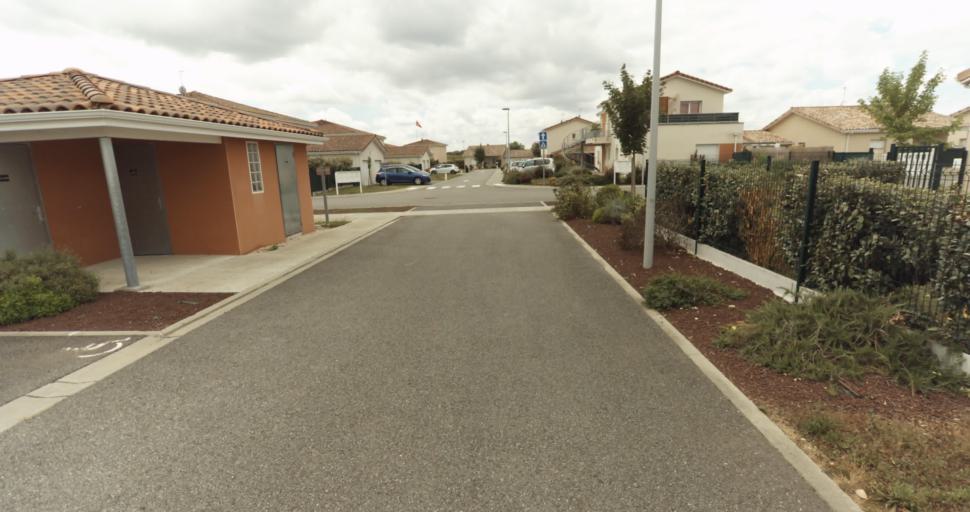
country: FR
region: Midi-Pyrenees
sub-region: Departement de la Haute-Garonne
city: Fontenilles
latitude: 43.5485
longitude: 1.1897
